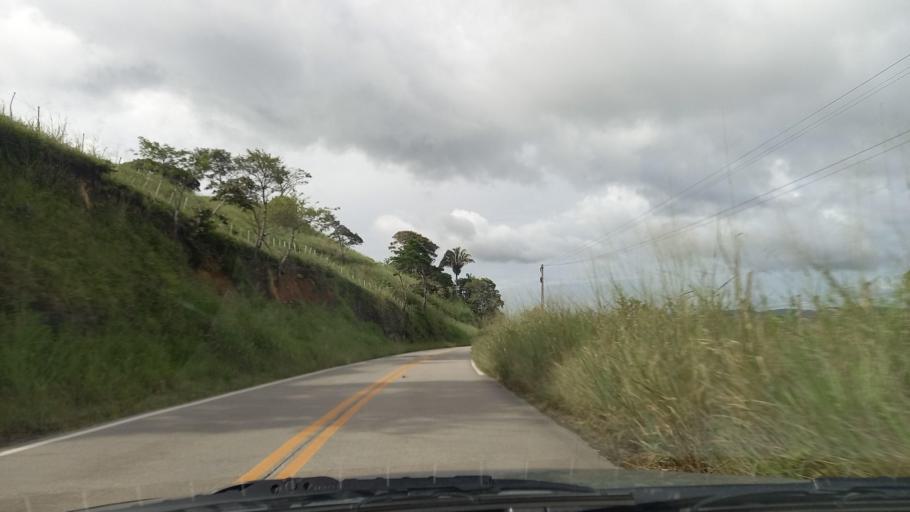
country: BR
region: Pernambuco
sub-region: Maraial
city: Maraial
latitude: -8.7883
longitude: -35.8797
